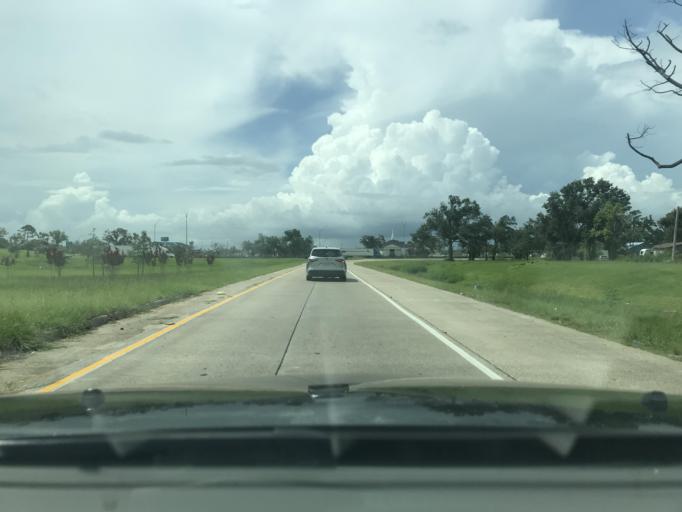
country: US
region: Louisiana
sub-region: Calcasieu Parish
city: Lake Charles
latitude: 30.2475
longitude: -93.1822
